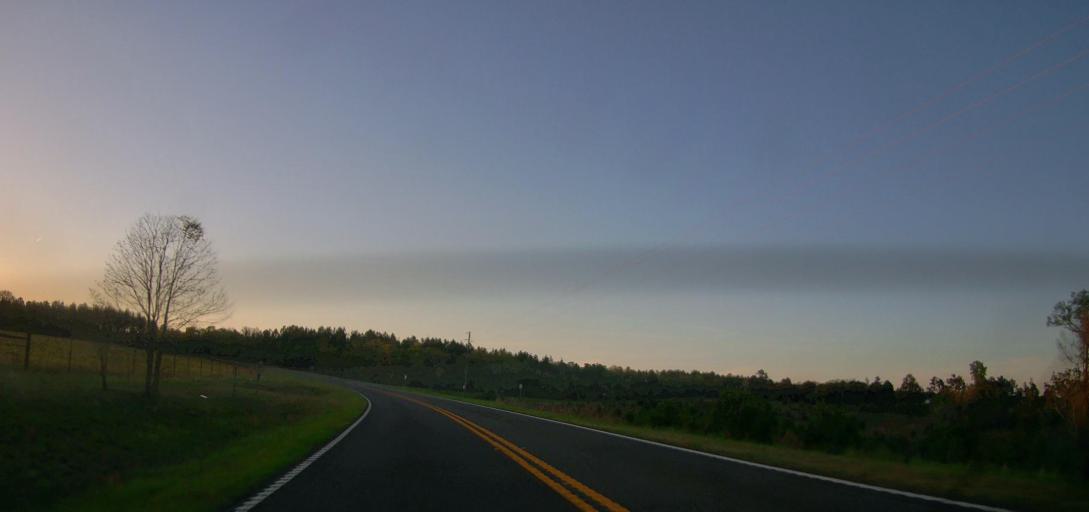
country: US
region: Georgia
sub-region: Marion County
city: Buena Vista
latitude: 32.4381
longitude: -84.6001
